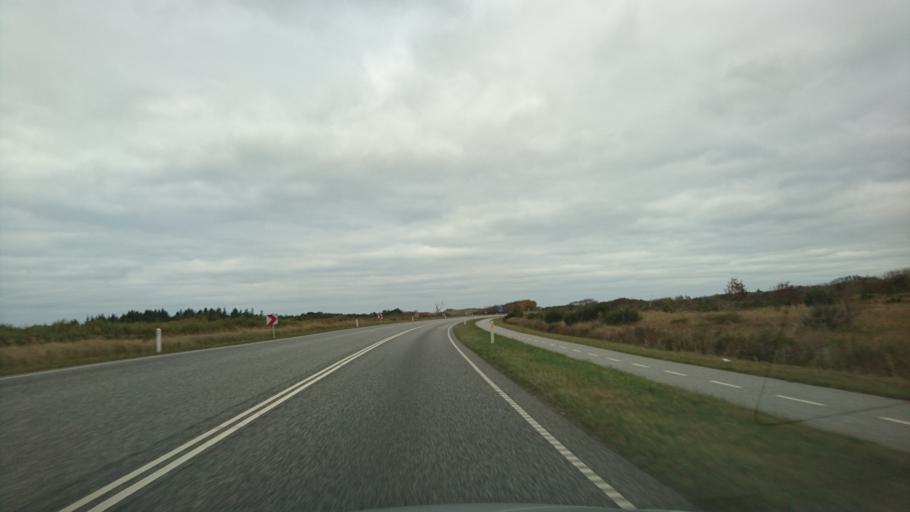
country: DK
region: North Denmark
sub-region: Frederikshavn Kommune
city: Skagen
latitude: 57.6702
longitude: 10.4544
